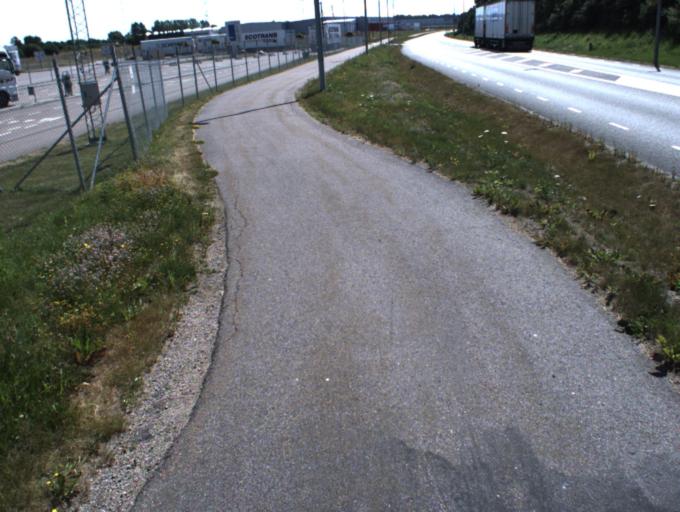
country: SE
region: Skane
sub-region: Helsingborg
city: Barslov
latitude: 56.0372
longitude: 12.7802
